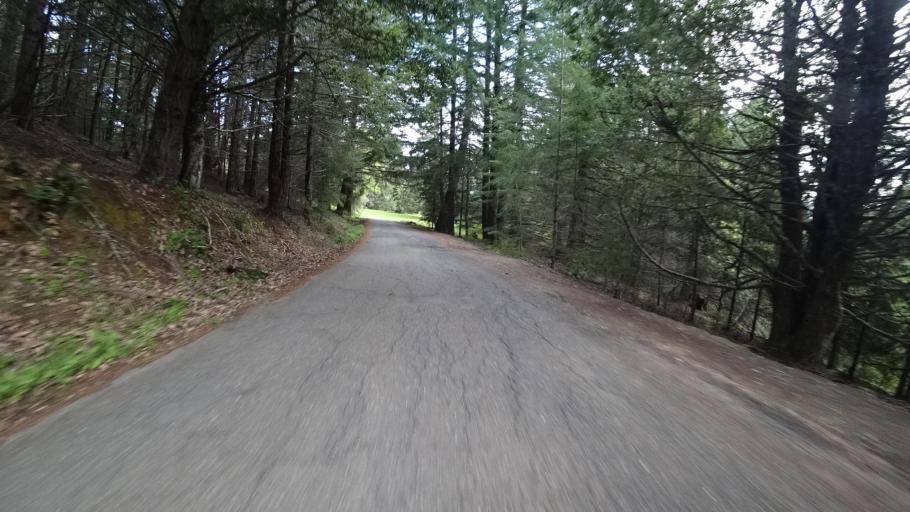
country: US
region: California
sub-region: Humboldt County
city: Redway
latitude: 40.2095
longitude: -123.6823
